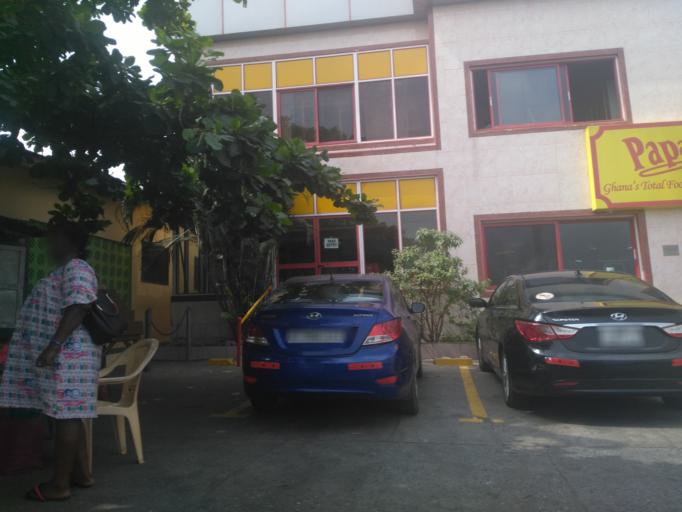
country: GH
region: Greater Accra
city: Dome
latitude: 5.6087
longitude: -0.2270
